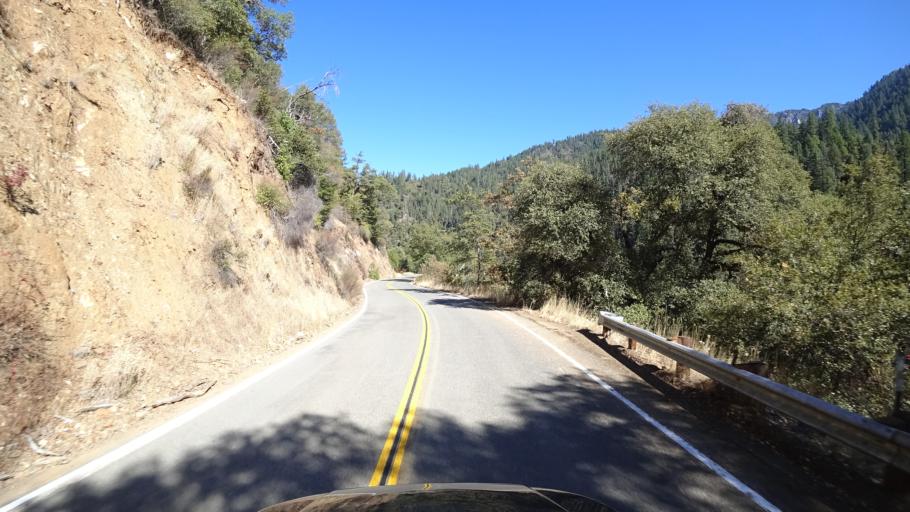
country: US
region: California
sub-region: Siskiyou County
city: Happy Camp
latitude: 41.3643
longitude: -123.4151
